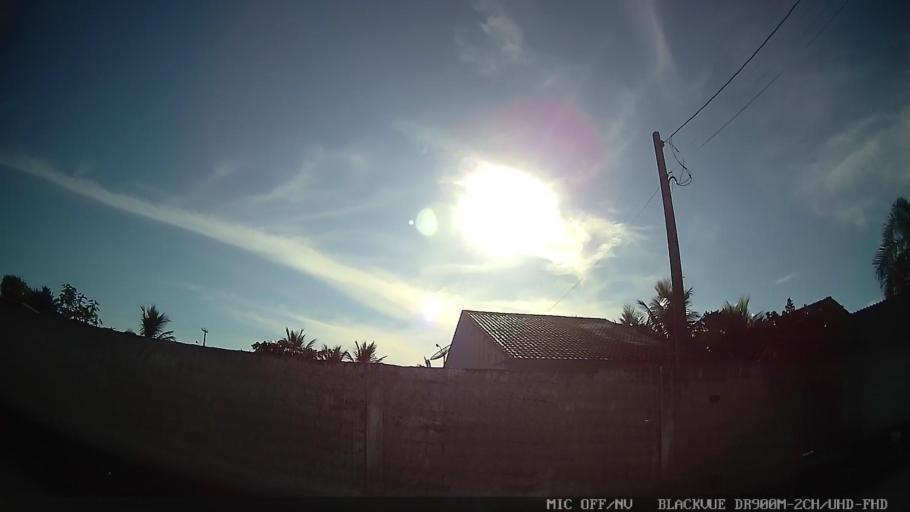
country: BR
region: Sao Paulo
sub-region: Iguape
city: Iguape
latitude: -24.7578
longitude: -47.5740
